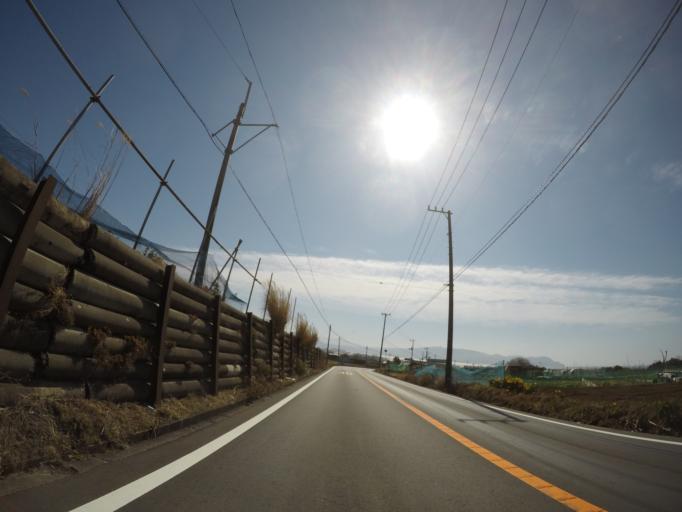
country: JP
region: Shizuoka
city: Numazu
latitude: 35.1342
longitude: 138.8360
